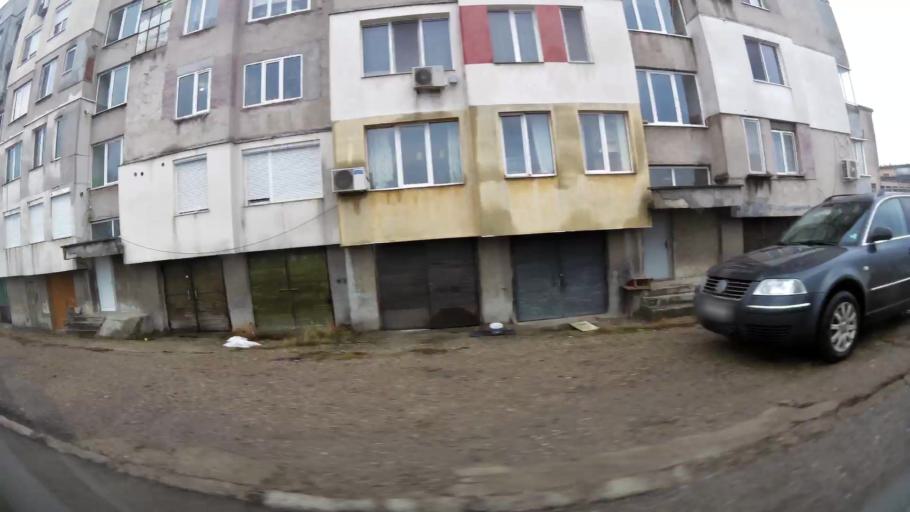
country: BG
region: Sofia-Capital
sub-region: Stolichna Obshtina
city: Sofia
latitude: 42.7429
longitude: 23.3438
